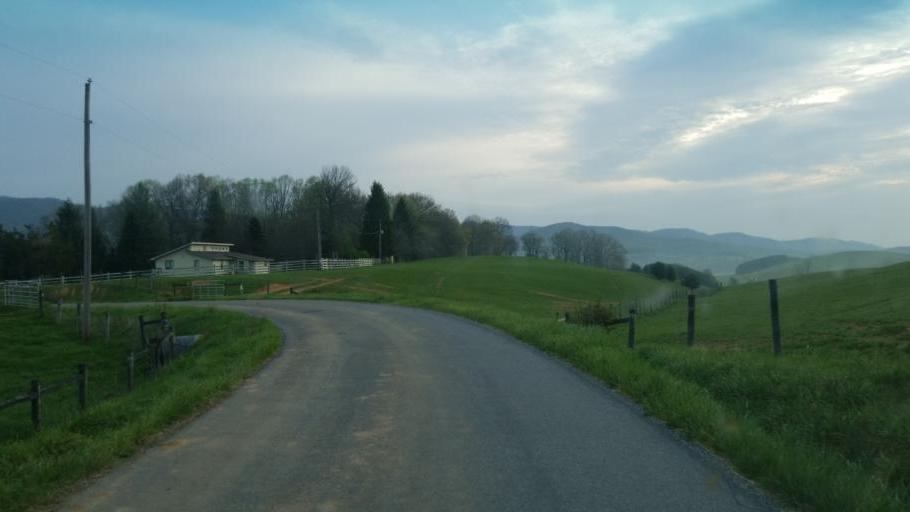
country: US
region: Virginia
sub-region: Smyth County
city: Marion
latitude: 36.7631
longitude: -81.4580
